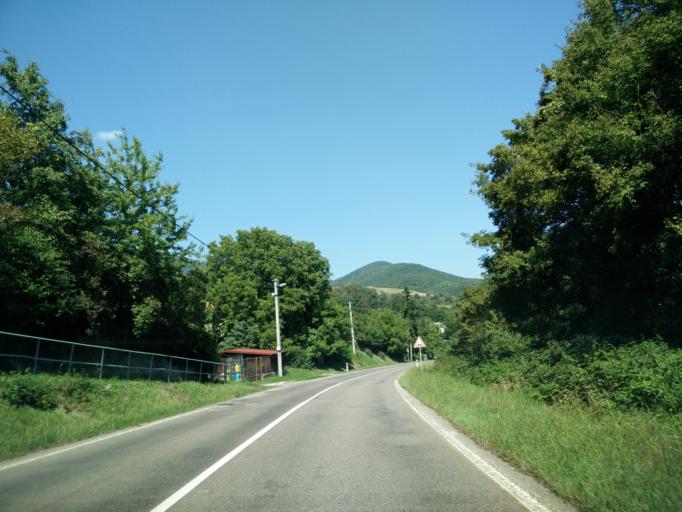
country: SK
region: Banskobystricky
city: Nova Bana
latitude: 48.3795
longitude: 18.5983
